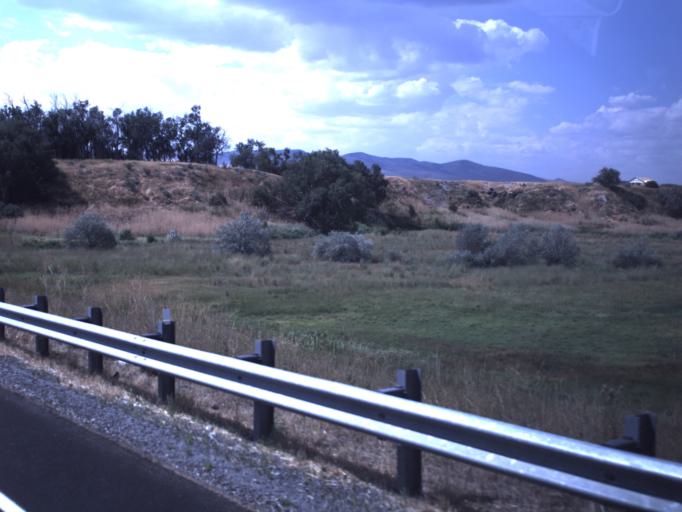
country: US
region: Utah
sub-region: Box Elder County
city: Garland
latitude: 41.7853
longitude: -112.1353
